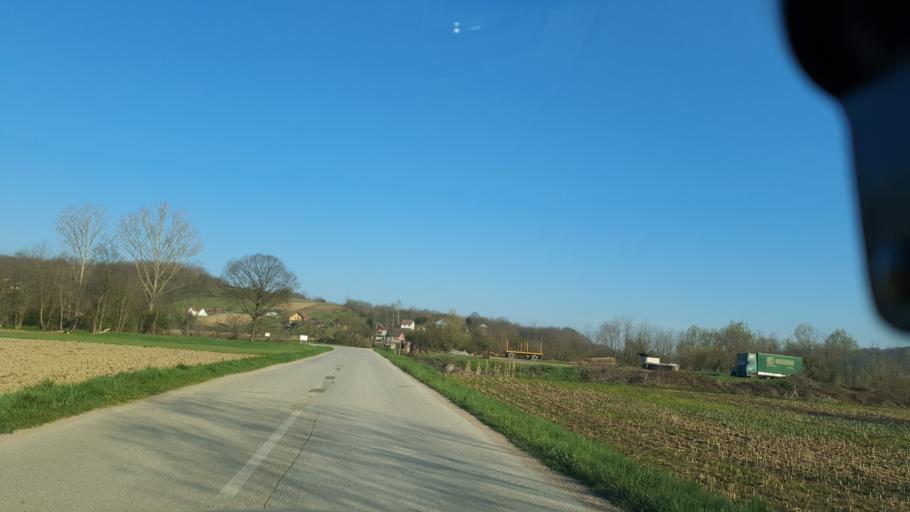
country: RS
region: Central Serbia
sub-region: Kolubarski Okrug
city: Osecina
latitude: 44.3866
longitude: 19.5699
